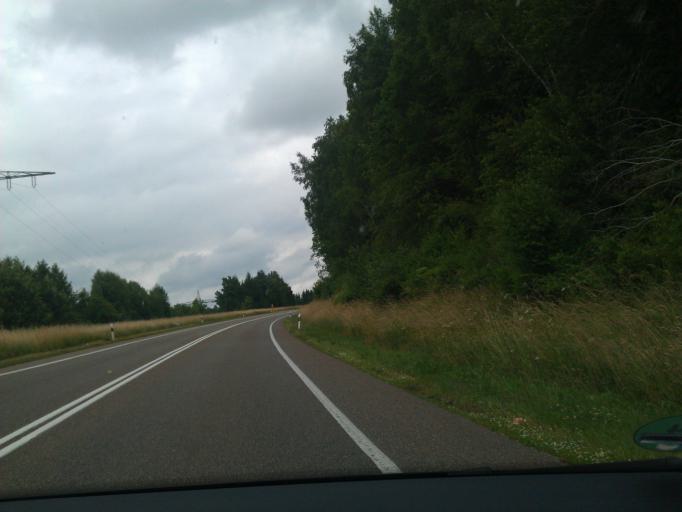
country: DE
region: Rheinland-Pfalz
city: Donsieders
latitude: 49.2621
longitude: 7.5959
